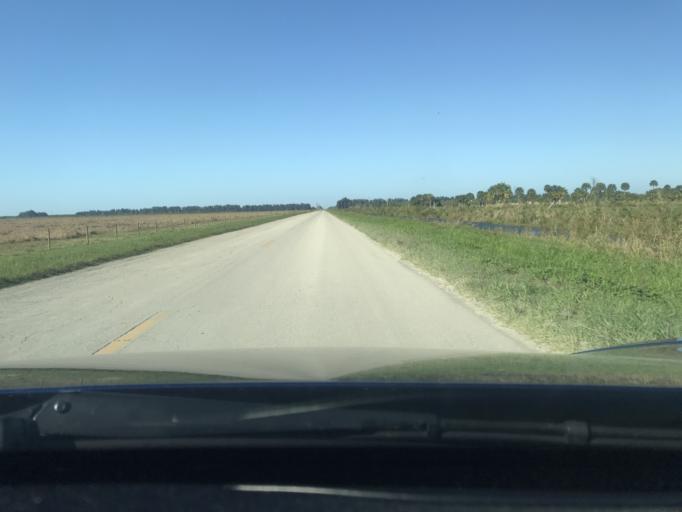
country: US
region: Florida
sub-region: Saint Lucie County
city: Lakewood Park
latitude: 27.4121
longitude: -80.4975
